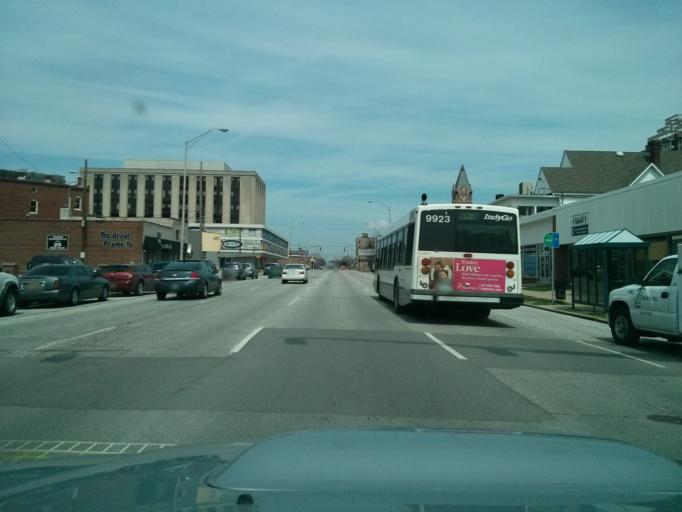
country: US
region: Indiana
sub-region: Marion County
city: Indianapolis
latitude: 39.7754
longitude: -86.1540
